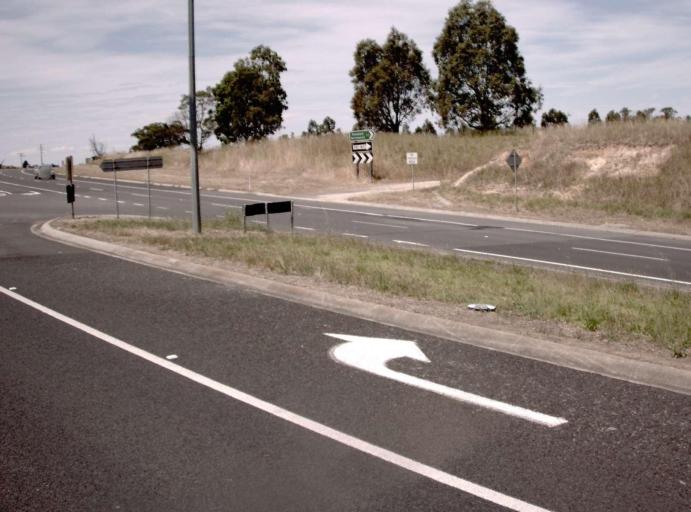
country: AU
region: Victoria
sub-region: Wellington
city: Heyfield
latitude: -38.1383
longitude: 146.7942
